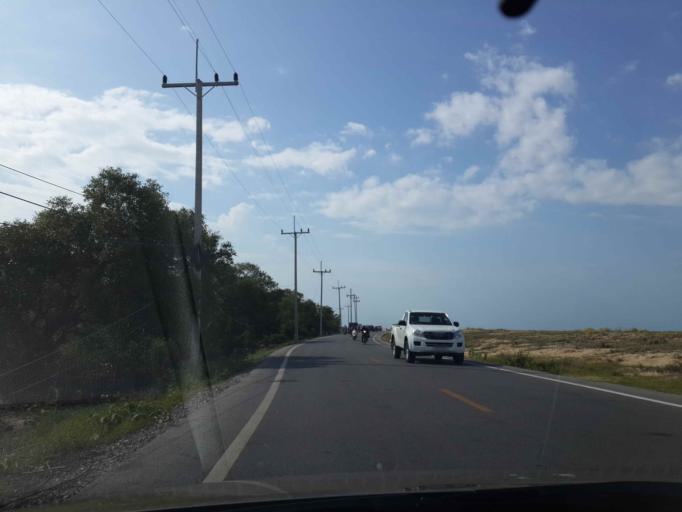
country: TH
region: Pattani
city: Yaring
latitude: 6.9219
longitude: 101.3306
